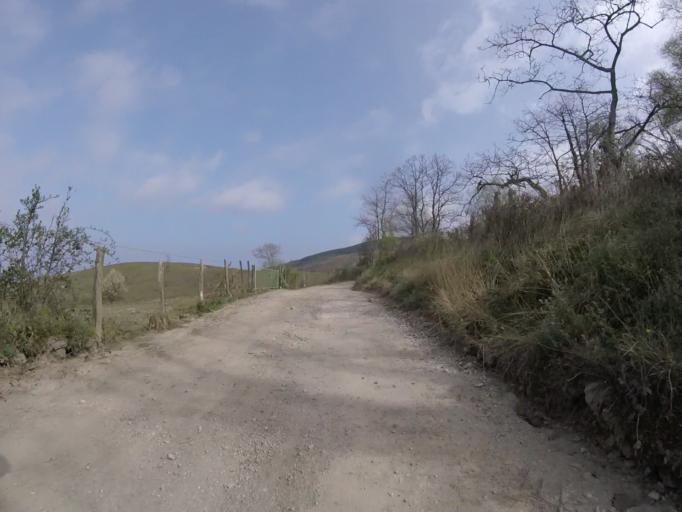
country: ES
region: Basque Country
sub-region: Provincia de Guipuzcoa
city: Zizurkil
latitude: 43.2377
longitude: -2.0821
